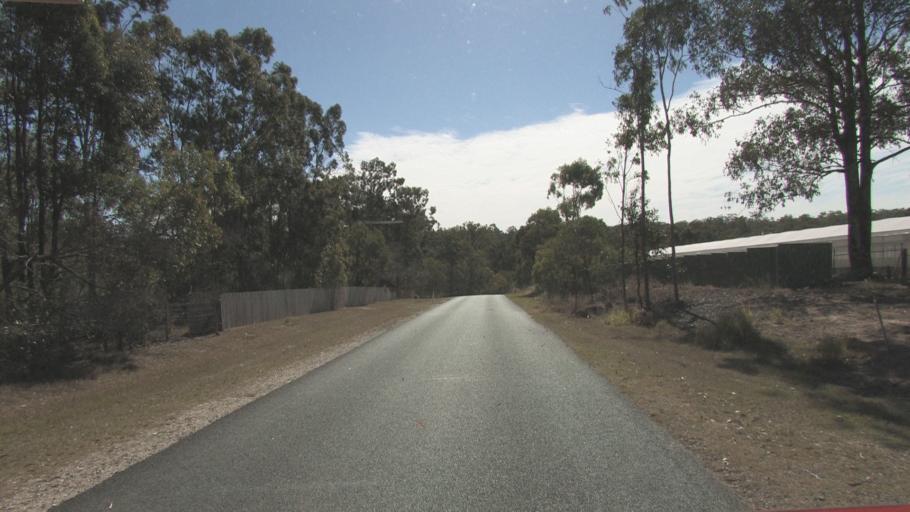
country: AU
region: Queensland
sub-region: Ipswich
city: Springfield Lakes
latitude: -27.7178
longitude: 152.9303
